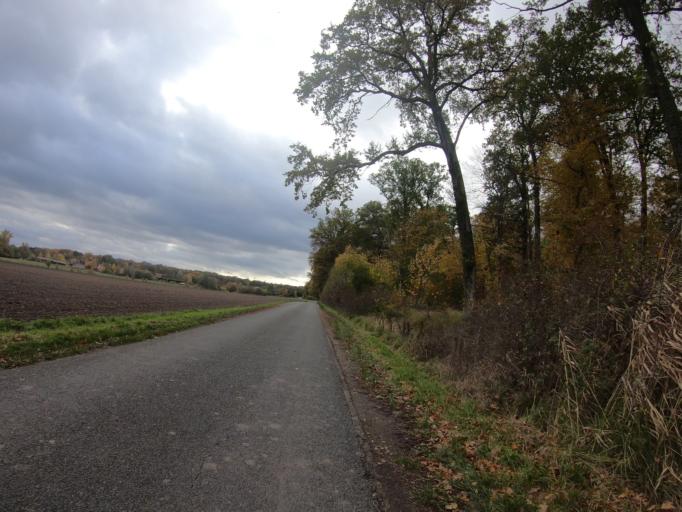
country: DE
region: Lower Saxony
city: Adenbuettel
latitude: 52.4069
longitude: 10.4742
